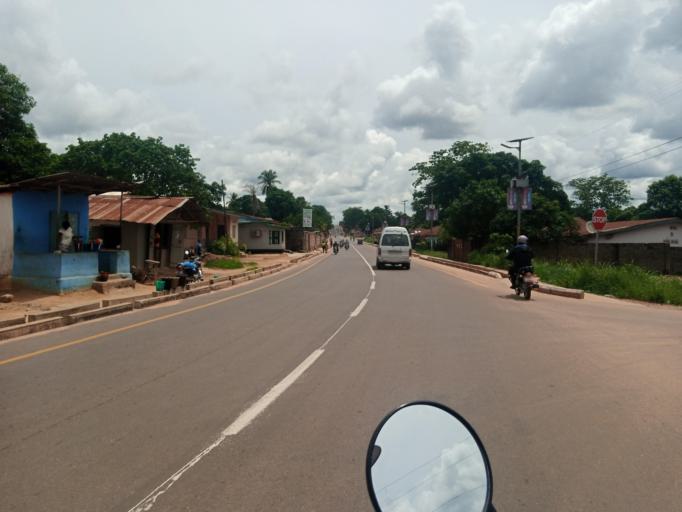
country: SL
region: Southern Province
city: Bo
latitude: 7.9564
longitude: -11.7215
